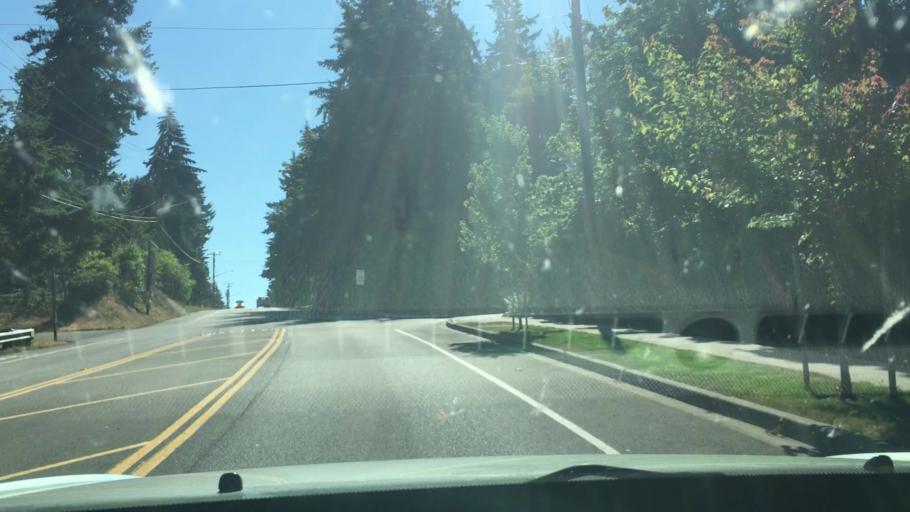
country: US
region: Washington
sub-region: King County
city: Newcastle
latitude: 47.5412
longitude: -122.1816
